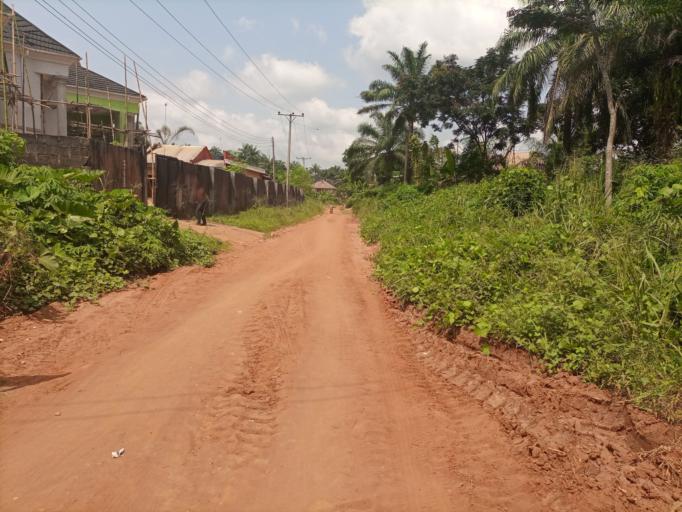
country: NG
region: Imo
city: Ihuo
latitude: 5.5284
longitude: 7.2608
